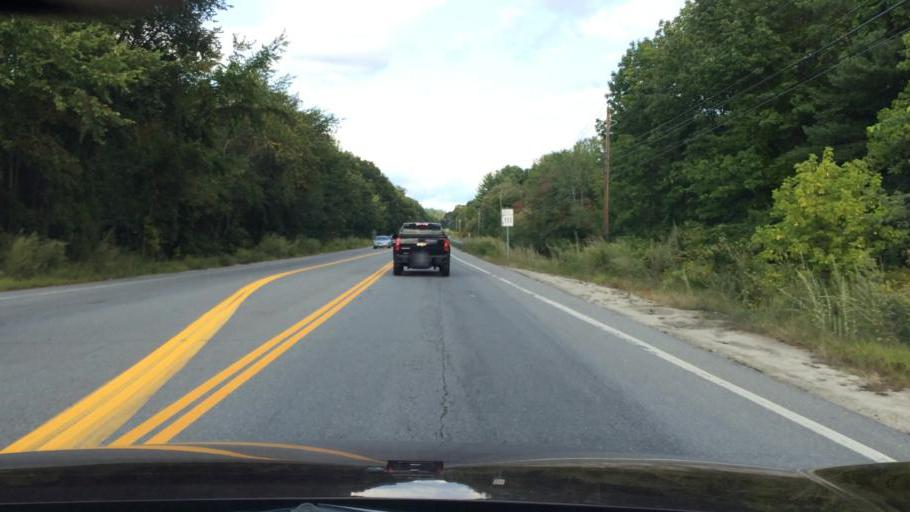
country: US
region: New Hampshire
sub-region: Hillsborough County
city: Hudson
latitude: 42.7721
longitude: -71.4071
